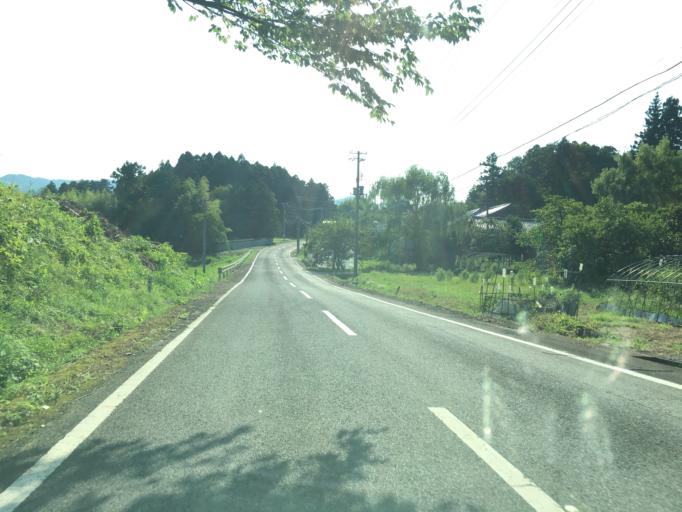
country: JP
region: Miyagi
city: Marumori
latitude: 37.8241
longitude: 140.9129
